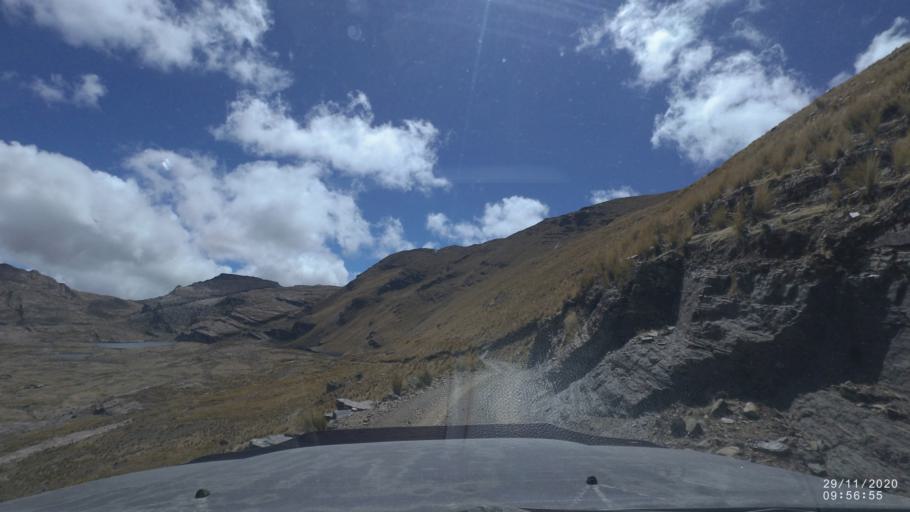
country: BO
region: Cochabamba
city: Cochabamba
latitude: -17.2708
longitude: -66.1717
